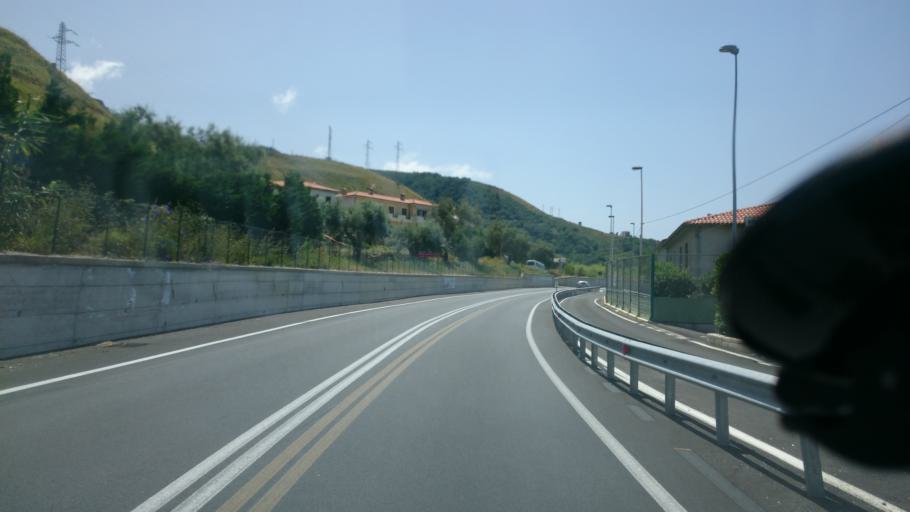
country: IT
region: Calabria
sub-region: Provincia di Cosenza
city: Cittadella del Capo
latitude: 39.5931
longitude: 15.8670
